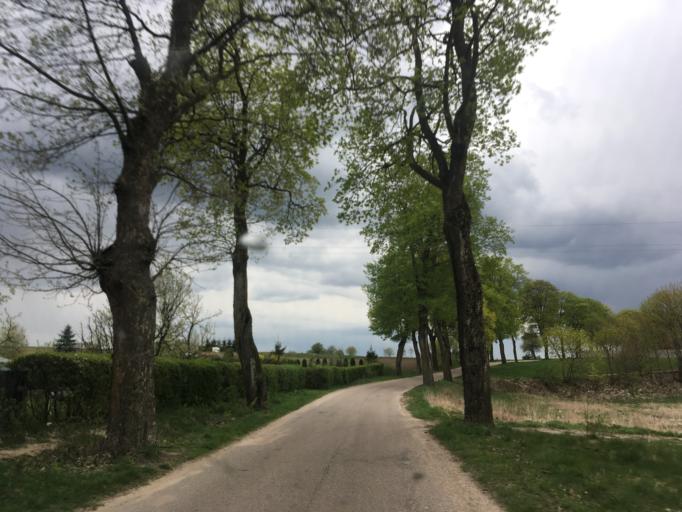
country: PL
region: Warmian-Masurian Voivodeship
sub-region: Powiat ostrodzki
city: Dabrowno
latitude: 53.4141
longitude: 20.1209
